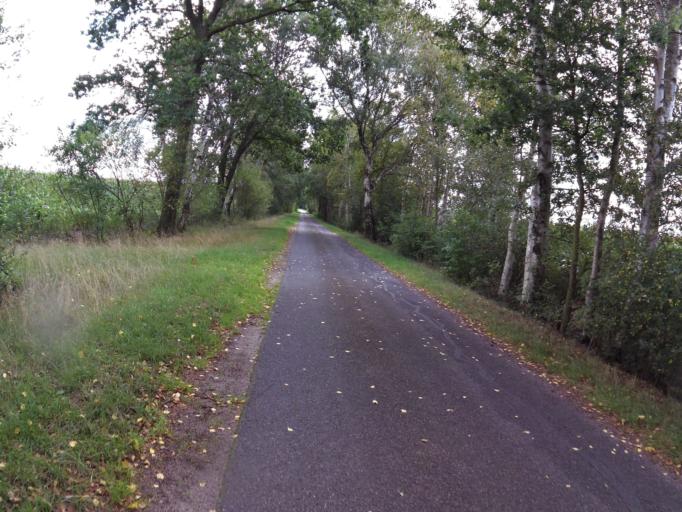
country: DE
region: Lower Saxony
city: Selsingen
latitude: 53.3665
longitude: 9.1609
